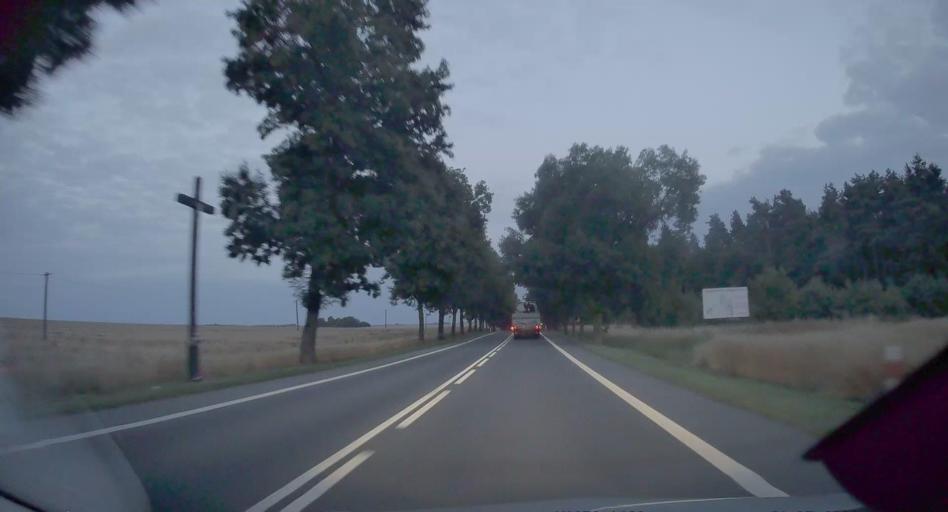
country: PL
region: Silesian Voivodeship
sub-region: Powiat klobucki
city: Opatow
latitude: 50.9445
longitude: 18.8346
